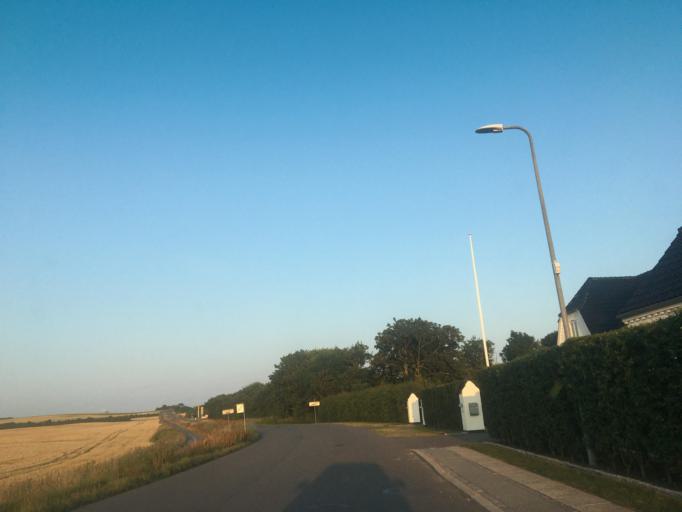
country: DK
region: North Denmark
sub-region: Thisted Kommune
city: Hurup
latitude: 56.7624
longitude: 8.3257
